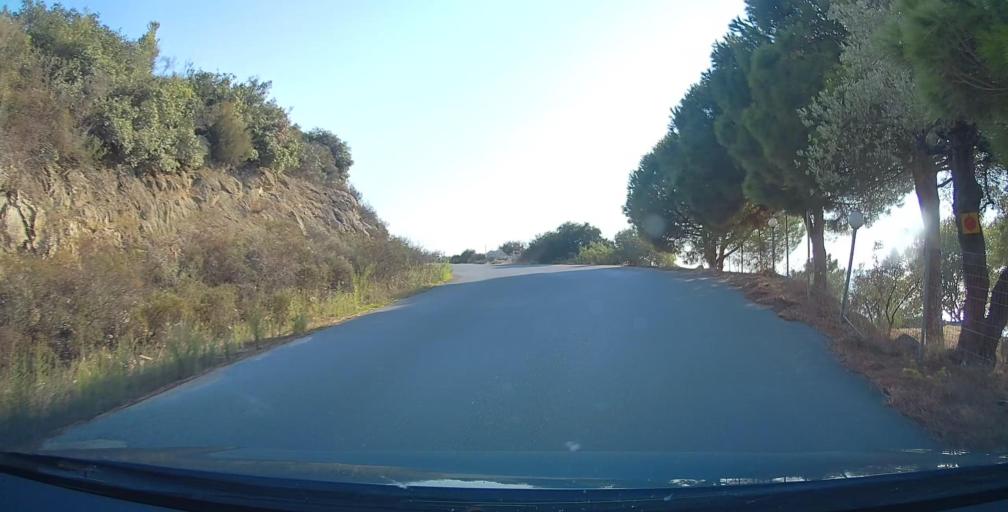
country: GR
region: Central Macedonia
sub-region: Nomos Chalkidikis
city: Sykia
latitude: 39.9945
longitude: 23.8928
